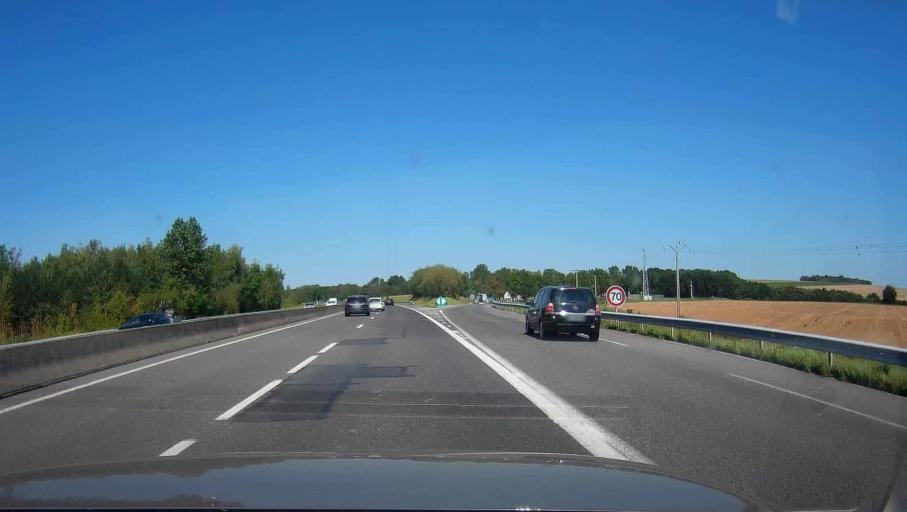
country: FR
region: Champagne-Ardenne
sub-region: Departement de la Marne
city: Fagnieres
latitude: 49.0045
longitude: 4.2988
